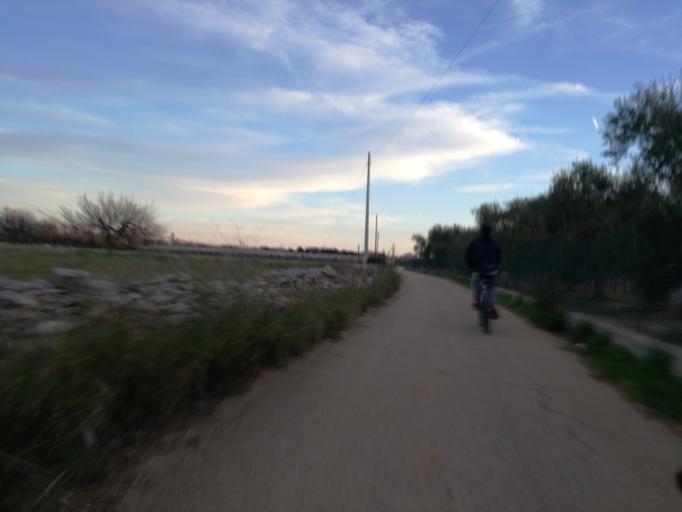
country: IT
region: Apulia
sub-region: Provincia di Bari
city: Adelfia
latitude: 41.0131
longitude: 16.8715
